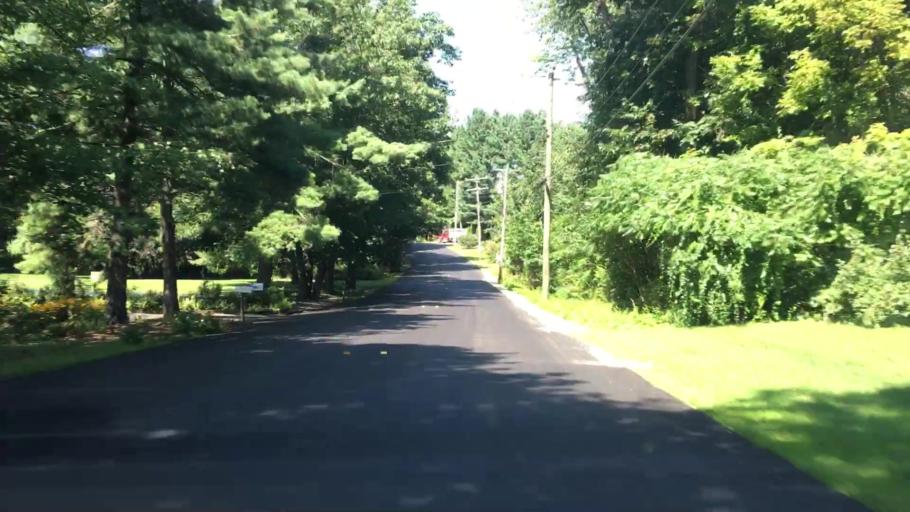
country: US
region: Maine
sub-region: York County
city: Eliot
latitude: 43.1686
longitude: -70.8401
